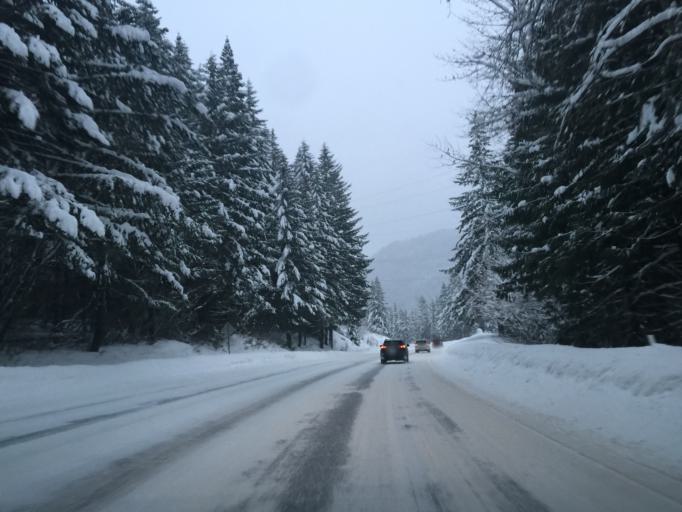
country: US
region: Washington
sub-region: Chelan County
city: Leavenworth
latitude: 47.7747
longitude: -120.9640
